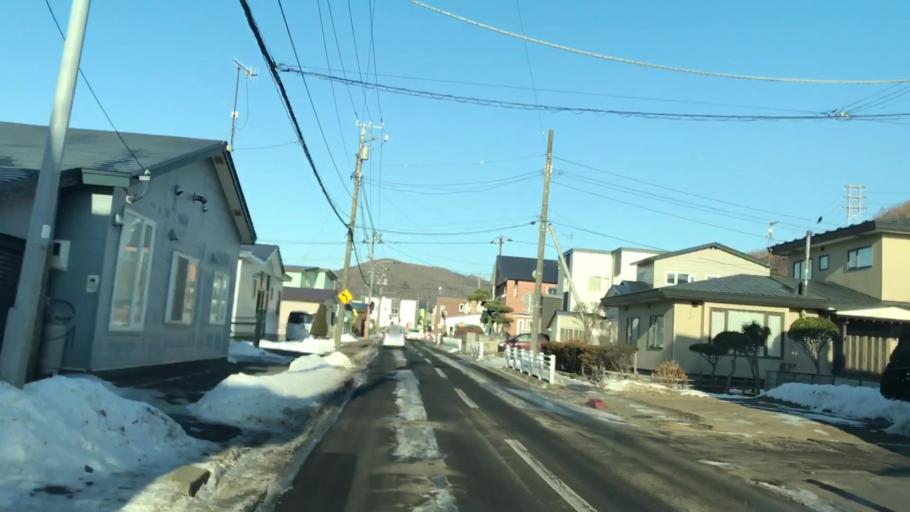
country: JP
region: Hokkaido
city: Muroran
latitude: 42.3650
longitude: 141.0429
